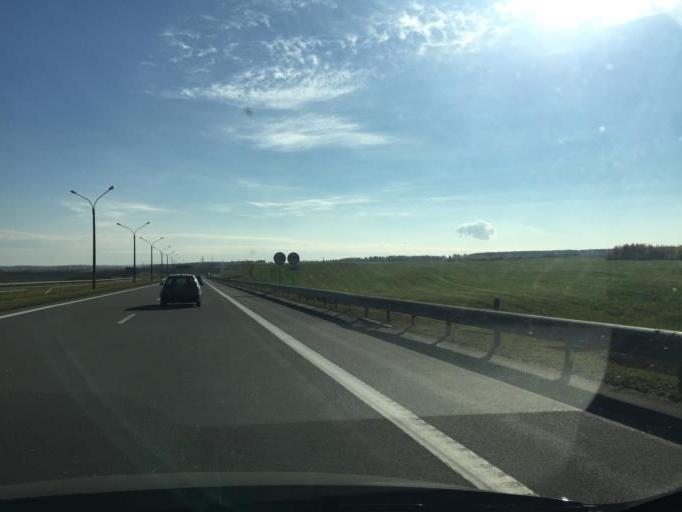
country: BY
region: Minsk
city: Slabada
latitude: 54.0107
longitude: 27.8989
